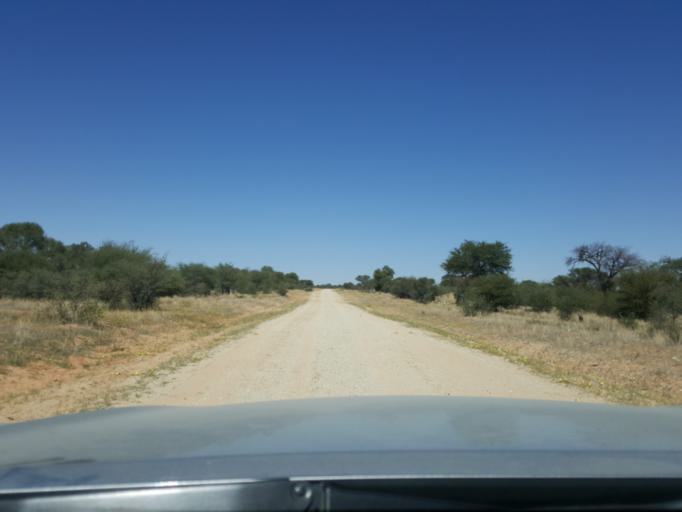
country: BW
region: Kgalagadi
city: Hukuntsi
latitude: -24.0824
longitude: 21.2263
